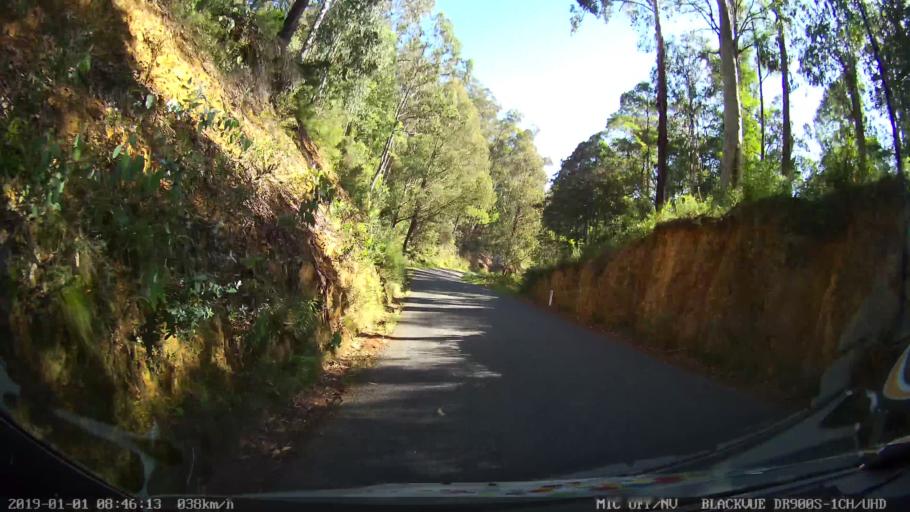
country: AU
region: New South Wales
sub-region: Snowy River
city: Jindabyne
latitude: -36.3014
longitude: 148.1924
